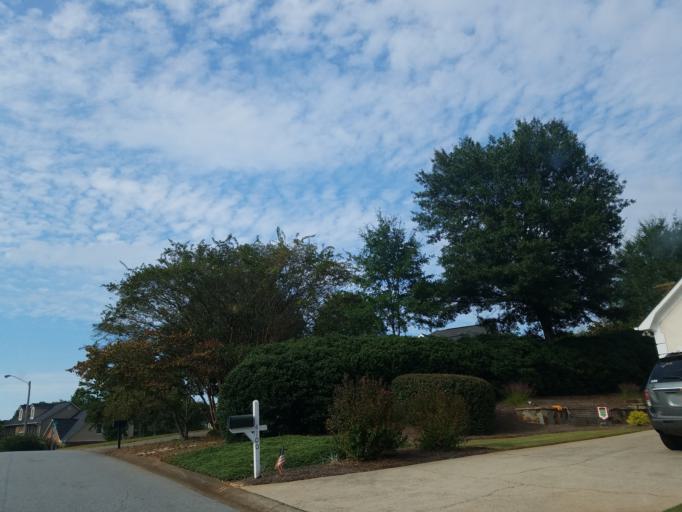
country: US
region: Georgia
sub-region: Cherokee County
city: Woodstock
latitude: 34.0453
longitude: -84.4962
